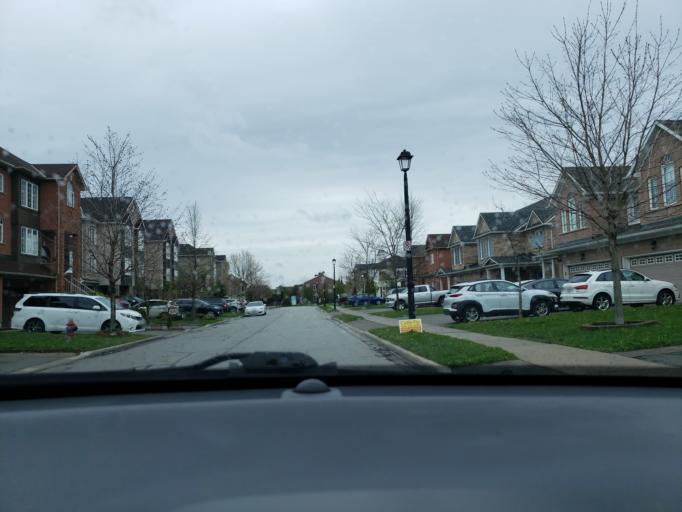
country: CA
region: Ontario
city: Newmarket
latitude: 44.0594
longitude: -79.4858
